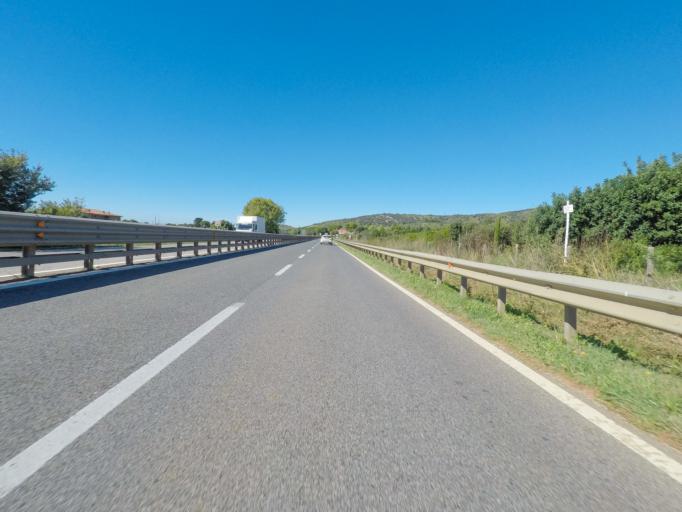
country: IT
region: Tuscany
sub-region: Provincia di Grosseto
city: Orbetello Scalo
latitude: 42.4334
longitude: 11.2824
